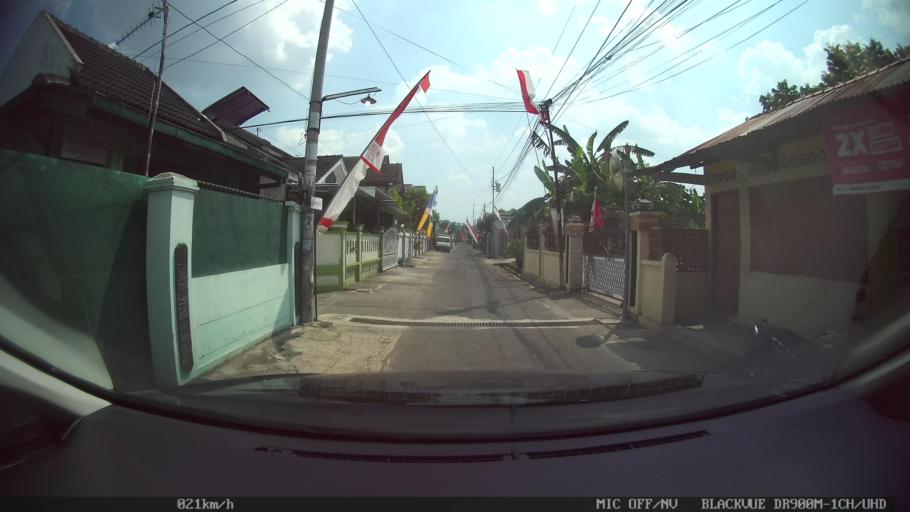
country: ID
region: Daerah Istimewa Yogyakarta
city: Yogyakarta
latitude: -7.8075
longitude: 110.4047
